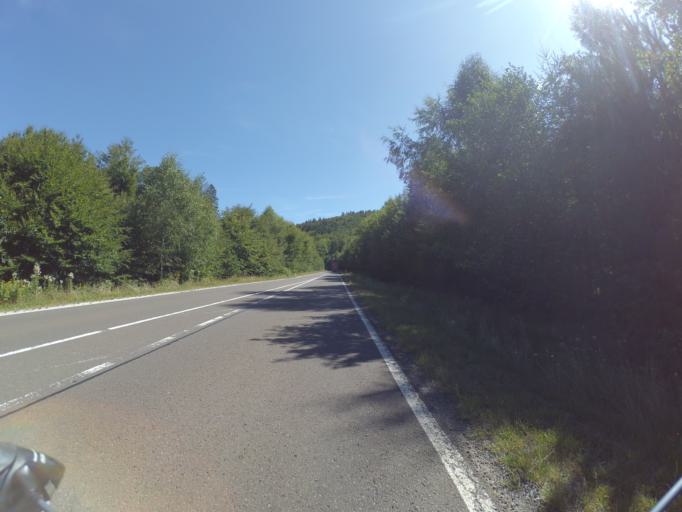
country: DE
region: Rheinland-Pfalz
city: Deuselbach
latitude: 49.7456
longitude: 7.0582
